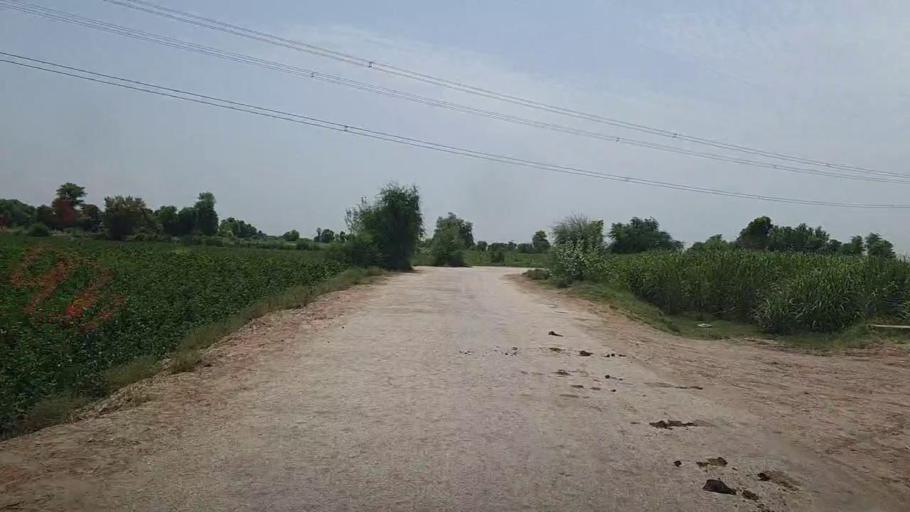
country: PK
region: Sindh
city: Pano Aqil
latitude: 27.8175
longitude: 69.2399
